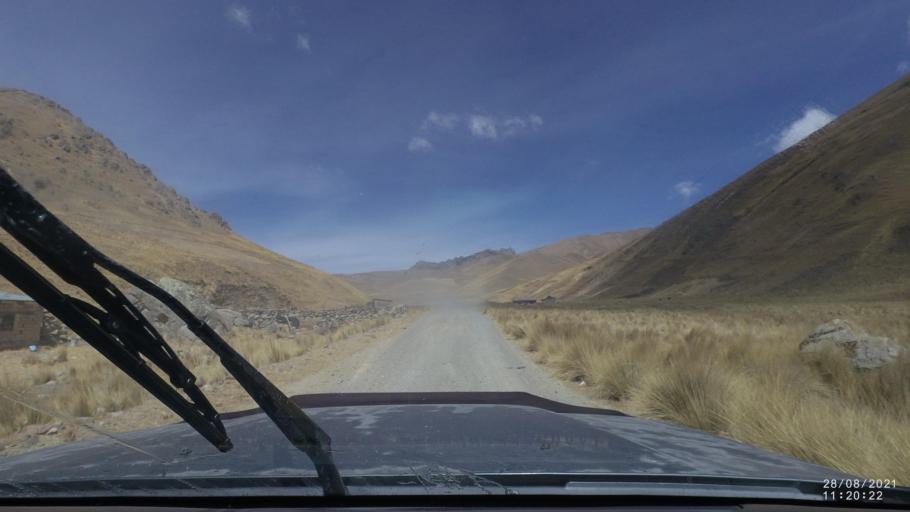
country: BO
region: Cochabamba
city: Cochabamba
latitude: -17.1581
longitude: -66.3399
